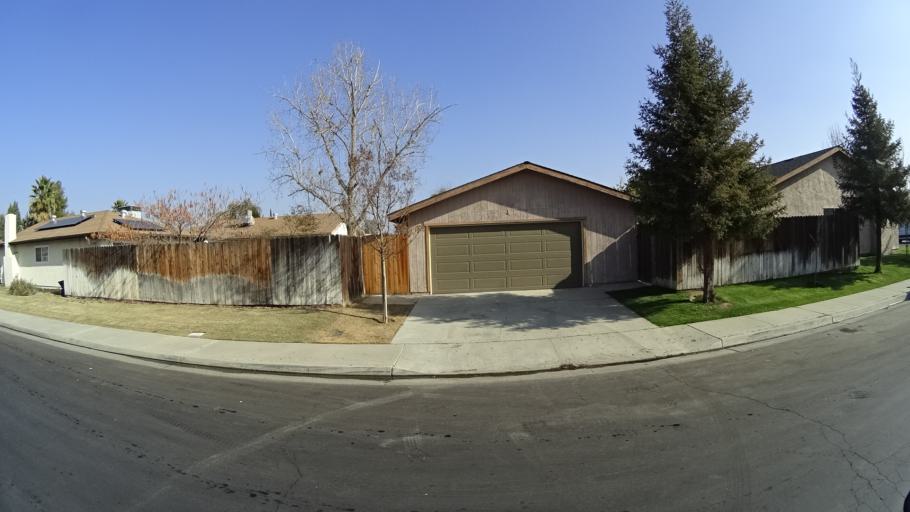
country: US
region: California
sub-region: Kern County
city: Bakersfield
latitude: 35.3264
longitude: -119.0627
